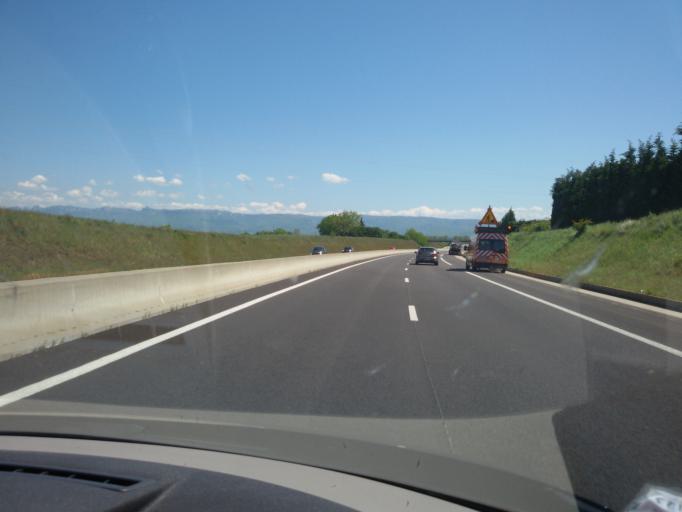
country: FR
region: Rhone-Alpes
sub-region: Departement de la Drome
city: Bourg-les-Valence
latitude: 44.9631
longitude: 4.9204
